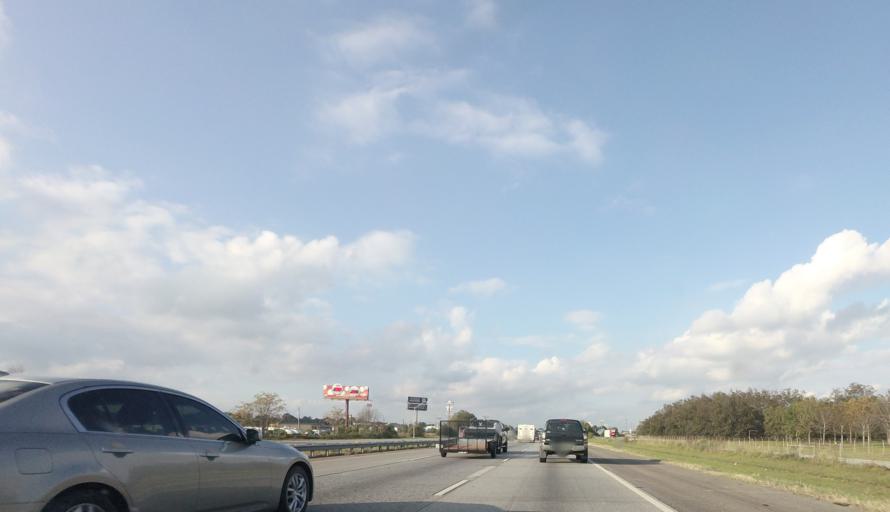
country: US
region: Georgia
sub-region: Peach County
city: Byron
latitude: 32.6543
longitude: -83.7439
